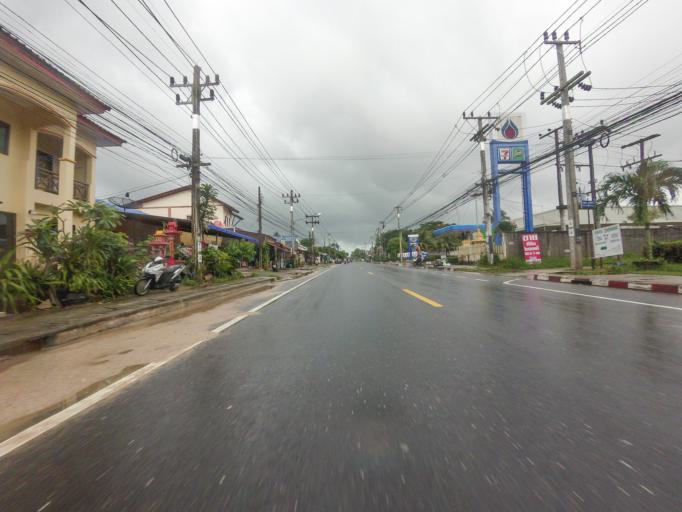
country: TH
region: Surat Thani
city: Ko Samui
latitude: 9.4480
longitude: 100.0050
